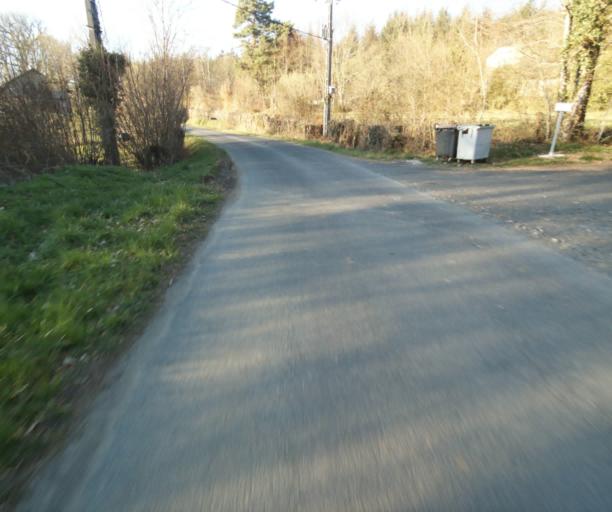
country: FR
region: Limousin
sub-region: Departement de la Correze
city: Seilhac
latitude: 45.3550
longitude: 1.7059
